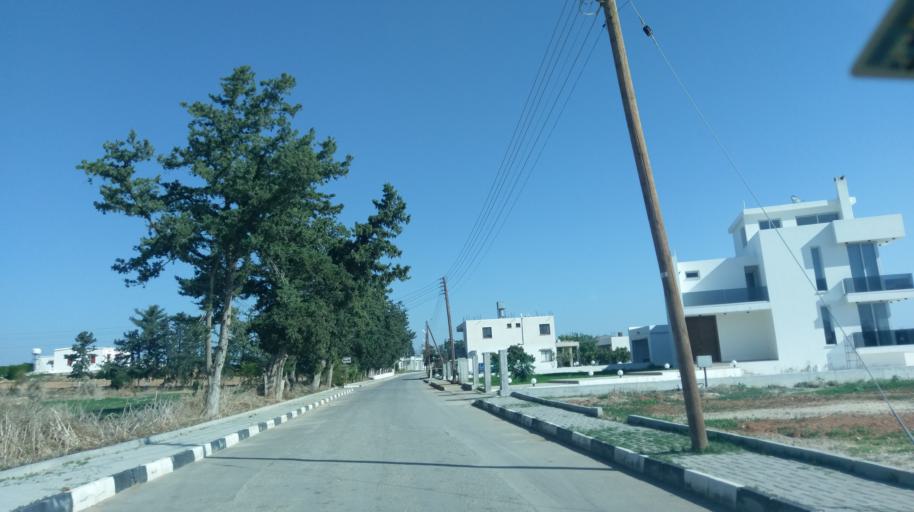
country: CY
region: Ammochostos
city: Leonarisso
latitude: 35.4106
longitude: 34.0007
